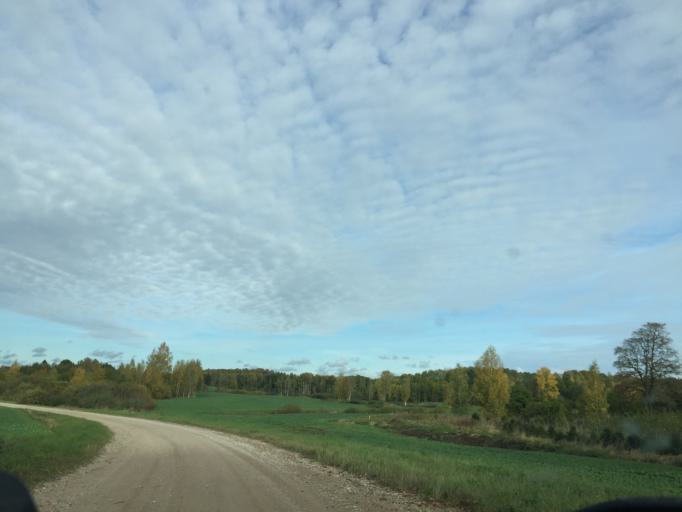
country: LV
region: Jaunpils
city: Jaunpils
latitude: 56.6173
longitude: 23.0677
